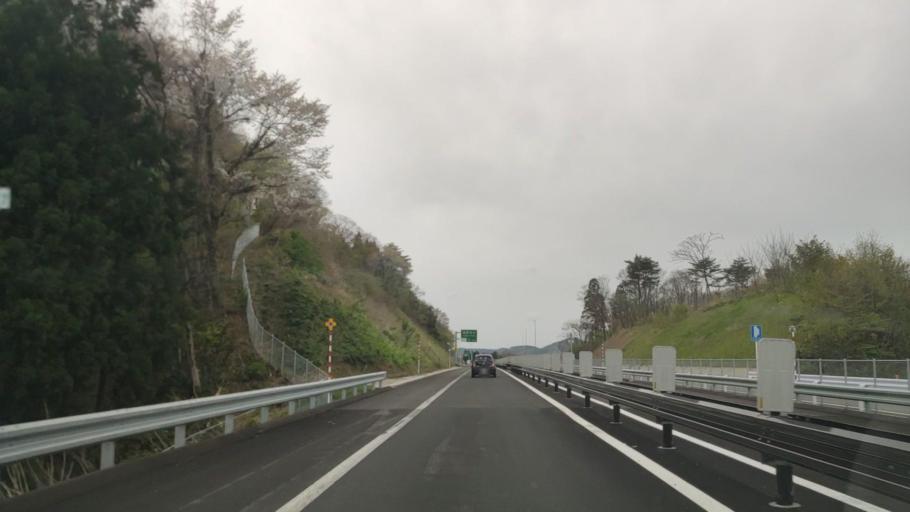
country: JP
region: Akita
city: Takanosu
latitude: 40.2058
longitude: 140.3202
